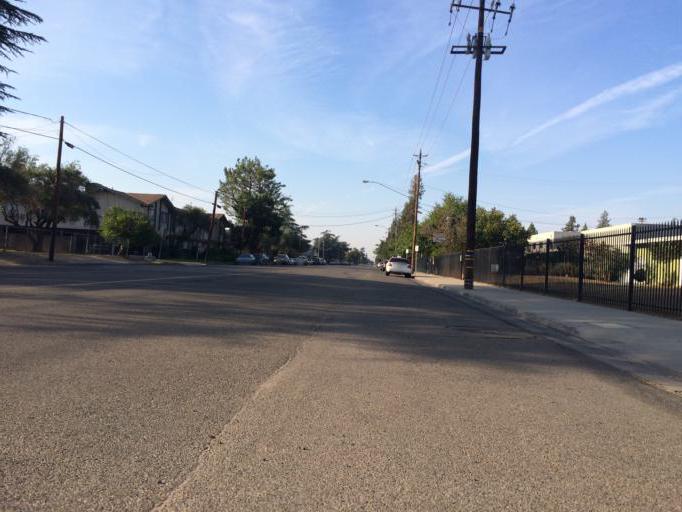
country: US
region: California
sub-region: Fresno County
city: Sunnyside
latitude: 36.7678
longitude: -119.7317
